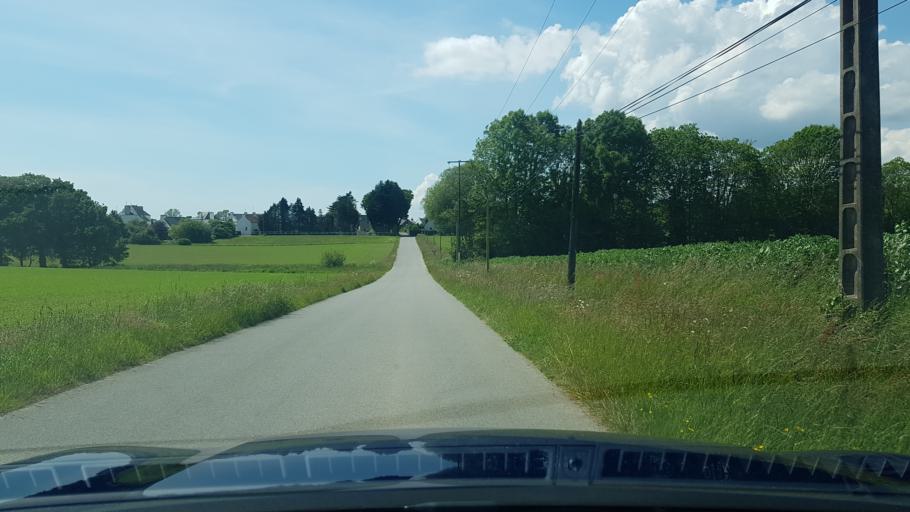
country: FR
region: Brittany
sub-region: Departement du Finistere
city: Clohars-Carnoet
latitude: 47.7931
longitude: -3.5766
